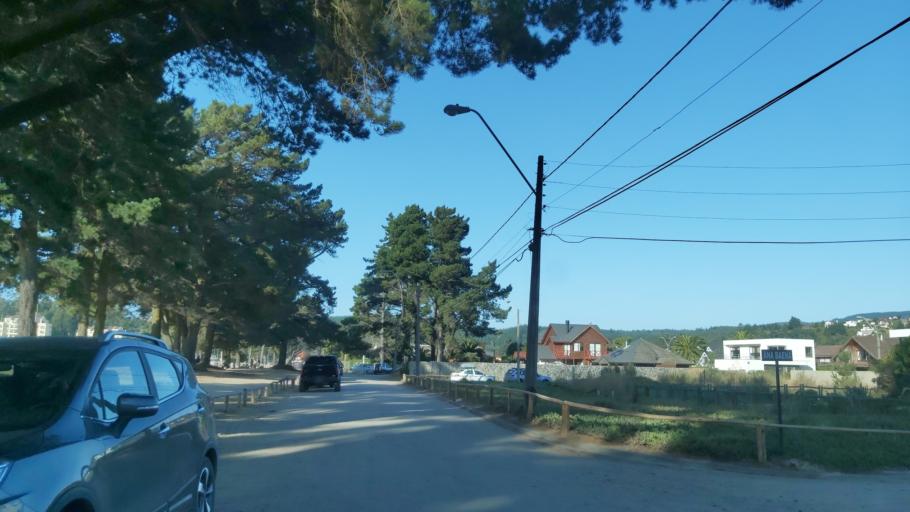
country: CL
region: Biobio
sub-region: Provincia de Concepcion
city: Tome
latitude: -36.5304
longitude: -72.9346
